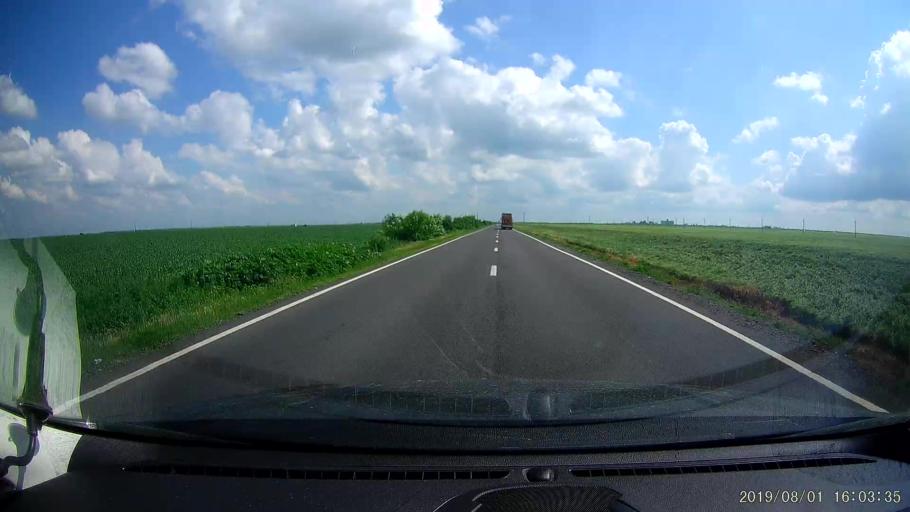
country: RO
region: Calarasi
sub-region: Comuna Dragalina
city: Drajna Noua
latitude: 44.4683
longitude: 27.3837
